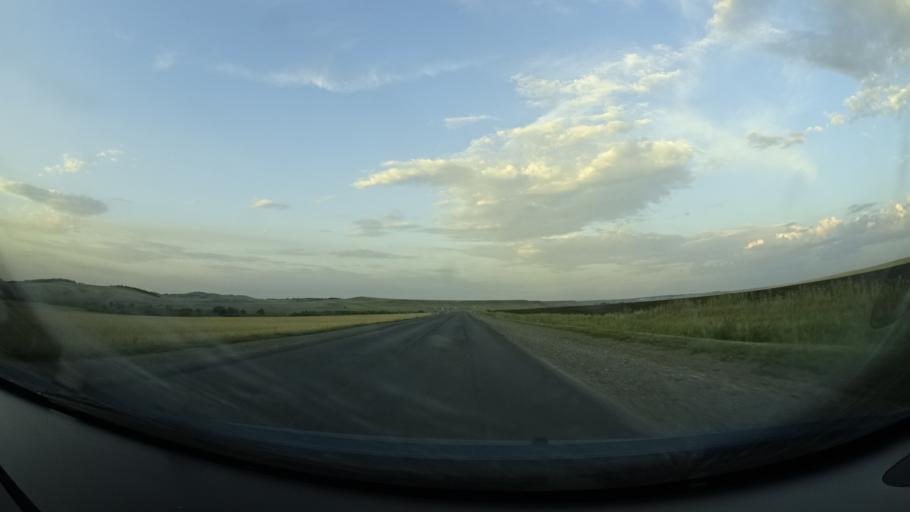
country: RU
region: Orenburg
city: Severnoye
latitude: 54.1282
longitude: 52.5745
